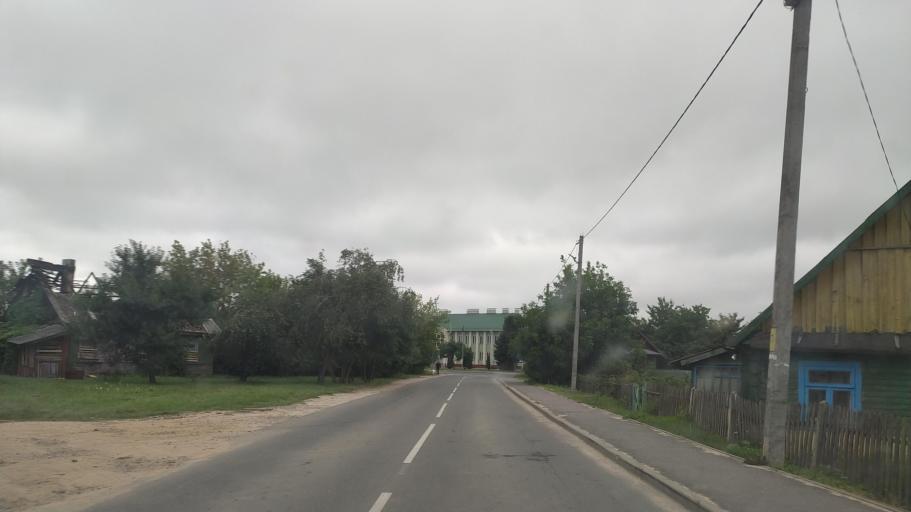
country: BY
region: Brest
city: Byaroza
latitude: 52.5294
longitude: 24.9701
